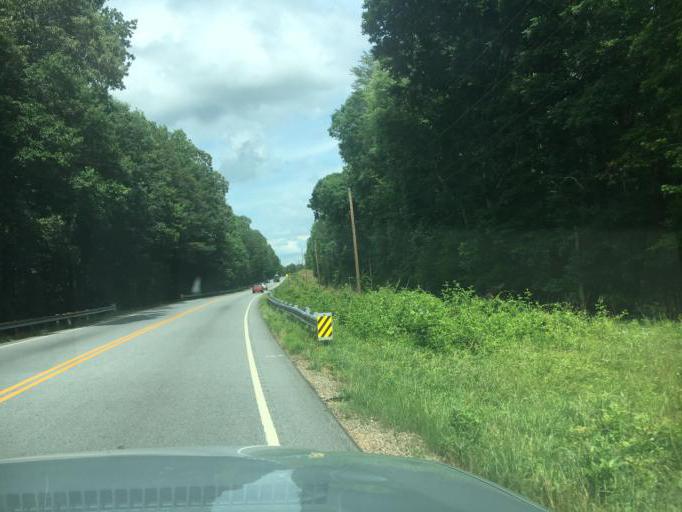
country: US
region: South Carolina
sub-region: Greenville County
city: Simpsonville
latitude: 34.6557
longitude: -82.2896
